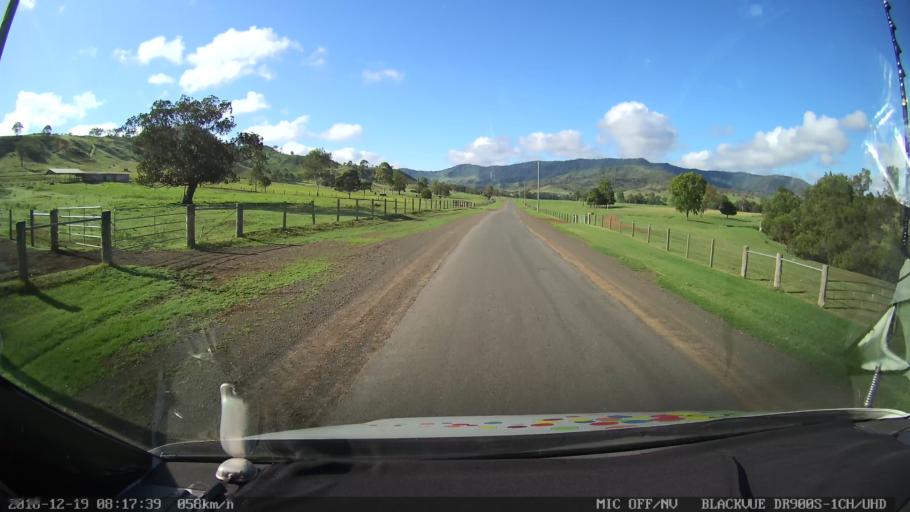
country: AU
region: New South Wales
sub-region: Kyogle
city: Kyogle
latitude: -28.2676
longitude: 152.9104
